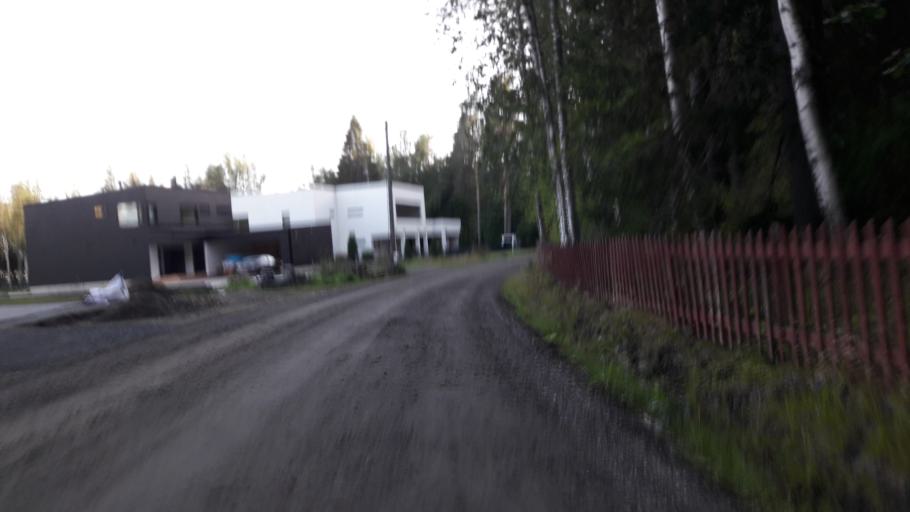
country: FI
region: North Karelia
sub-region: Joensuu
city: Joensuu
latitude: 62.6148
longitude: 29.6988
